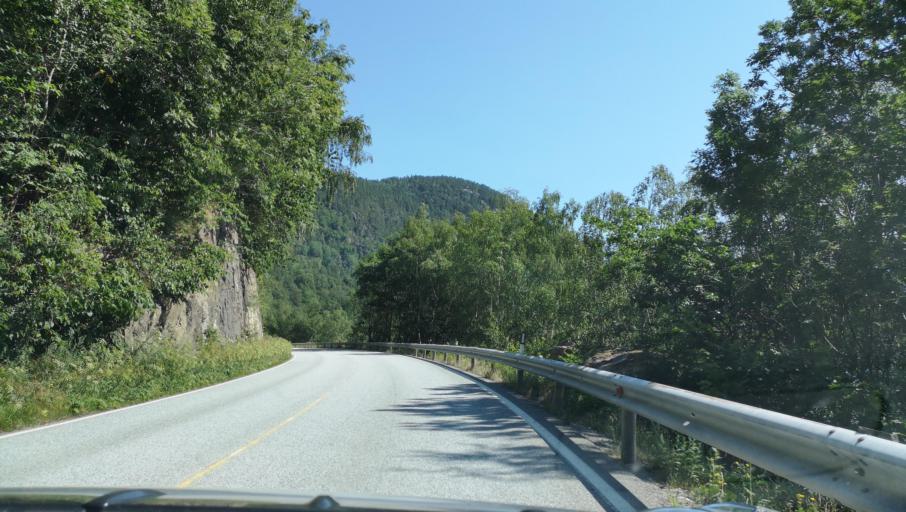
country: NO
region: Hordaland
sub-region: Ulvik
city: Ulvik
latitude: 60.4895
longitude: 6.8516
